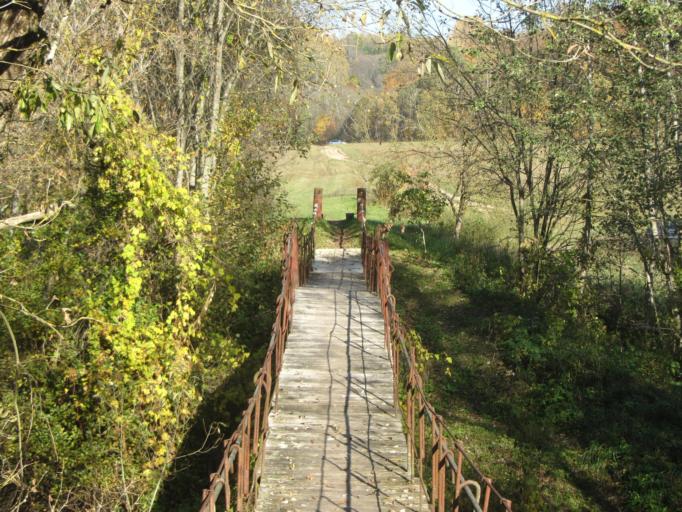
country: LT
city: Ariogala
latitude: 55.3530
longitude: 23.3496
